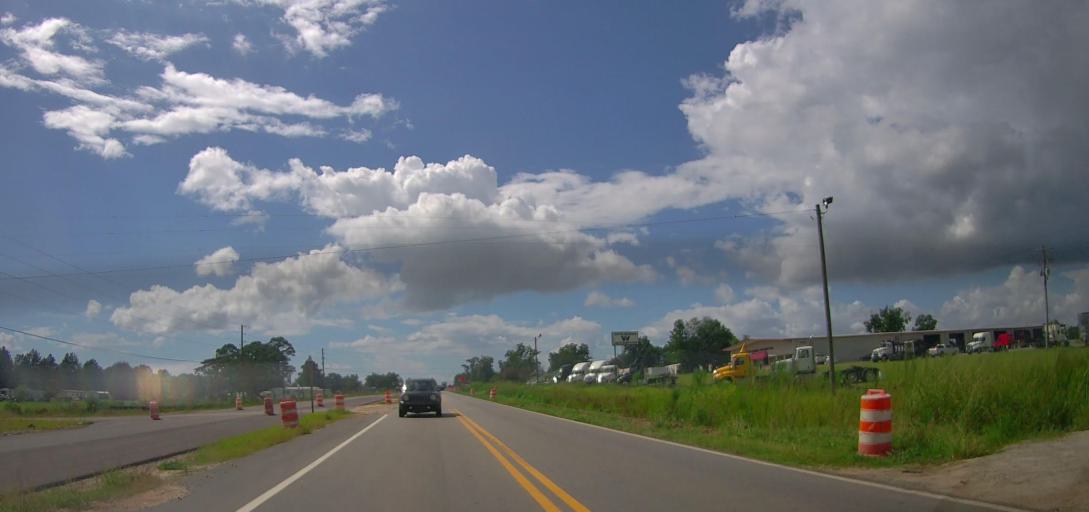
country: US
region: Georgia
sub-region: Coffee County
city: Douglas
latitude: 31.5350
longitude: -82.9179
